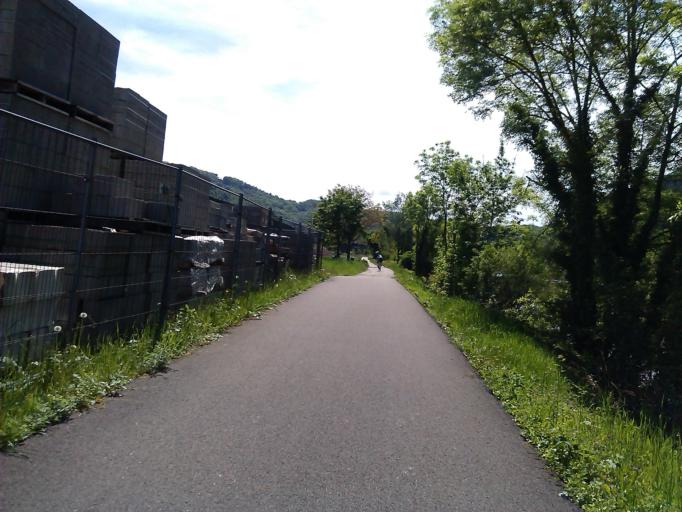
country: FR
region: Franche-Comte
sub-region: Departement du Doubs
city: Beure
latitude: 47.2139
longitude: 6.0011
